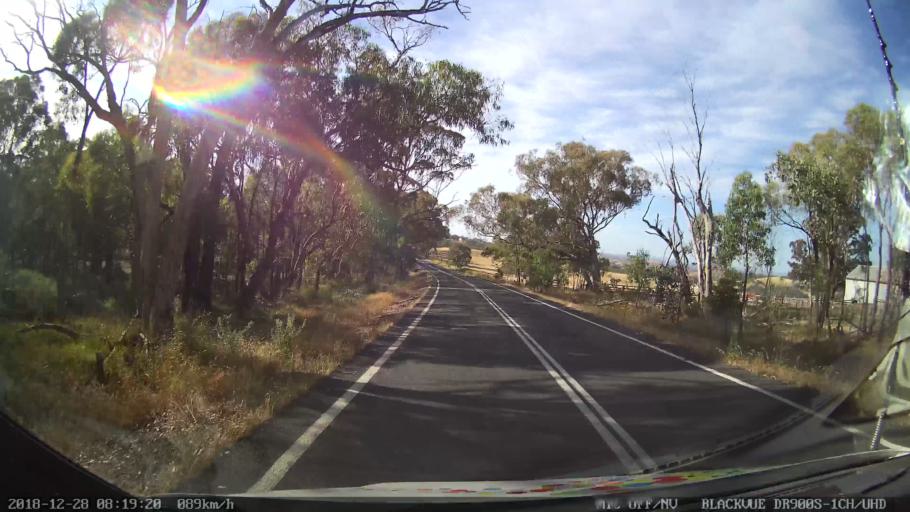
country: AU
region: New South Wales
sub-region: Blayney
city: Blayney
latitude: -33.8577
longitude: 149.3507
